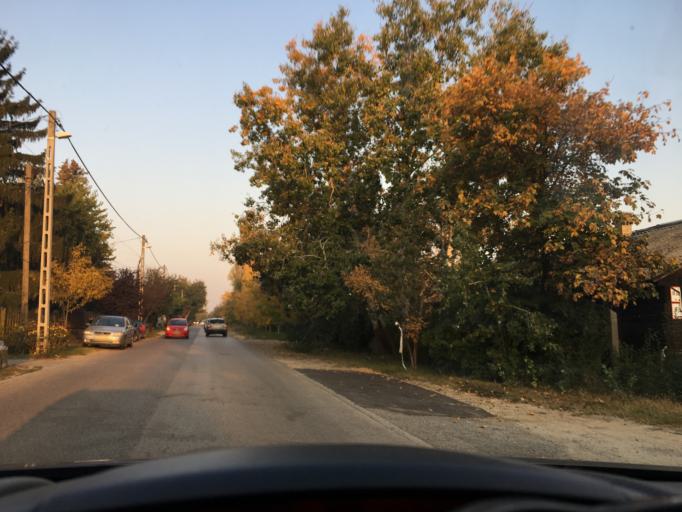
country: HU
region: Budapest
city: Budapest XVII. keruelet
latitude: 47.4750
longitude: 19.2520
